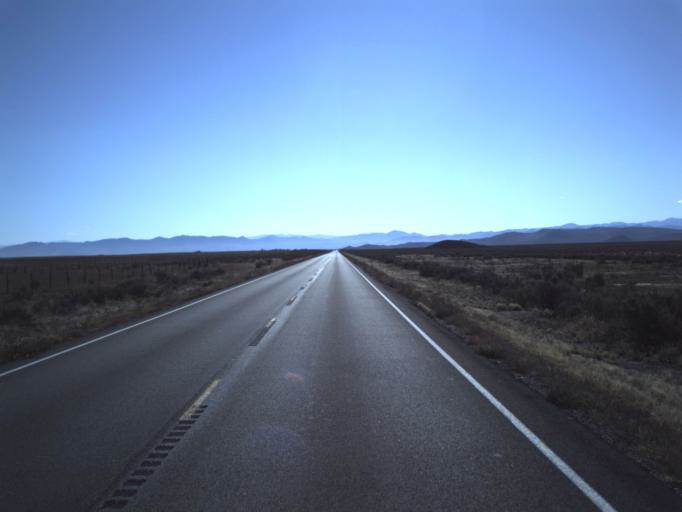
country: US
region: Utah
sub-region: Washington County
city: Enterprise
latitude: 37.7809
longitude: -113.8598
